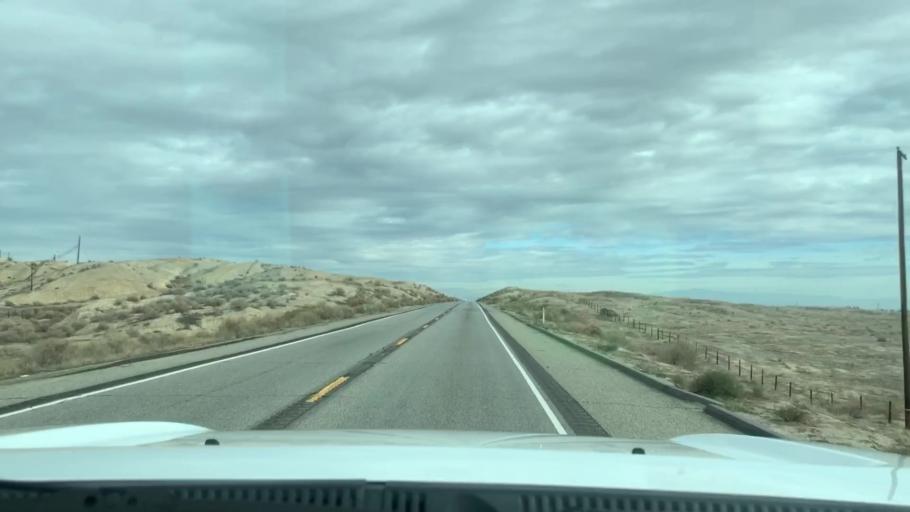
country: US
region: California
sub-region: Kern County
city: Ford City
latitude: 35.2342
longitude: -119.3678
